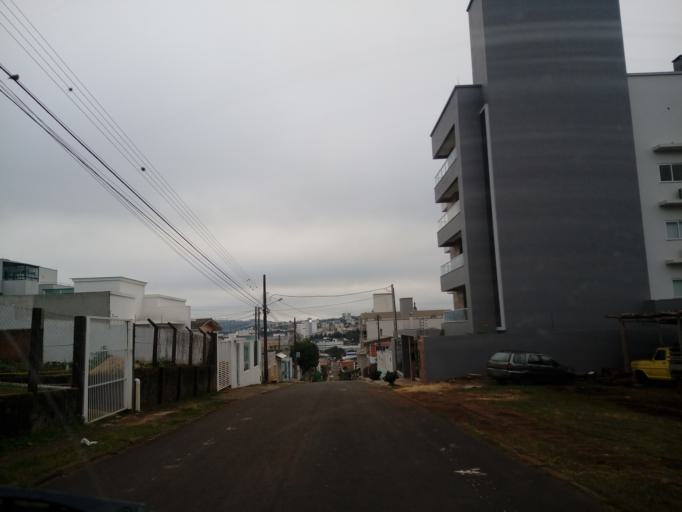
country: BR
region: Santa Catarina
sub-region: Chapeco
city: Chapeco
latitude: -27.0900
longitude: -52.6279
